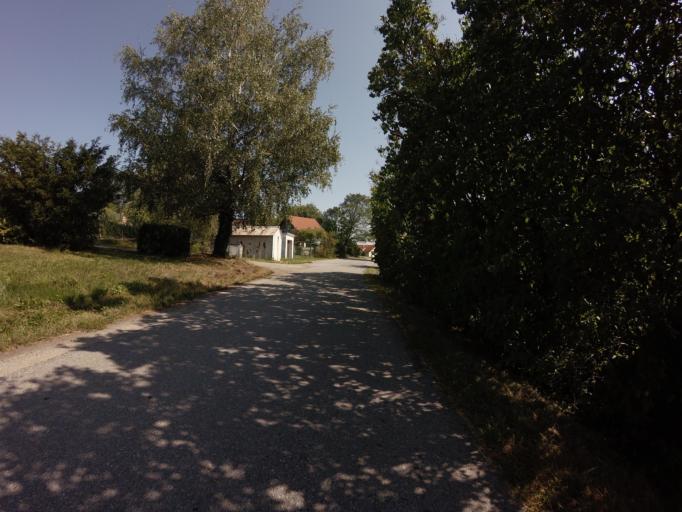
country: CZ
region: Jihocesky
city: Kamenny Ujezd
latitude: 48.8745
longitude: 14.3785
